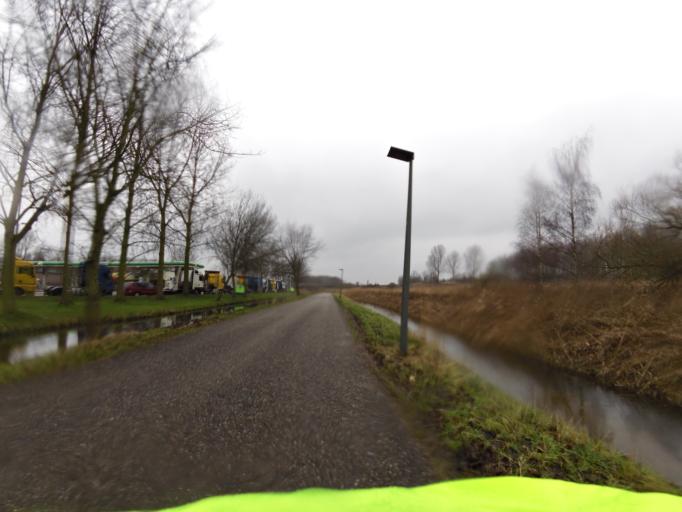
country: NL
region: South Holland
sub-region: Gemeente Vlaardingen
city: Vlaardingen
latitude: 51.9192
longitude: 4.3169
